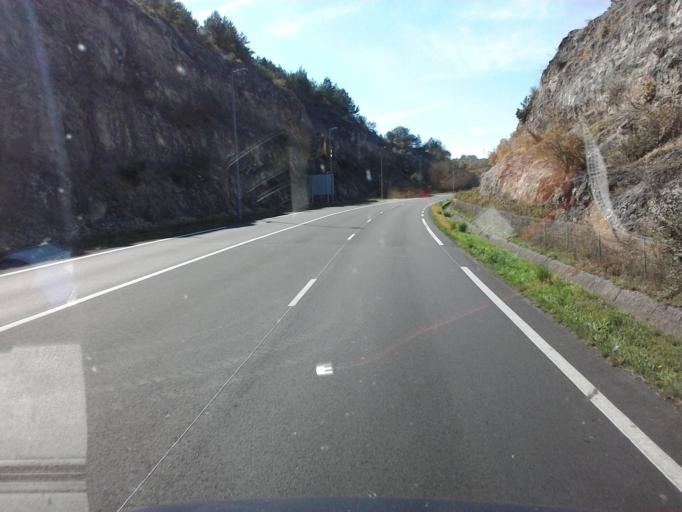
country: FR
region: Bourgogne
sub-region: Departement de l'Yonne
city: Tonnerre
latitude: 47.8502
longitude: 3.9898
